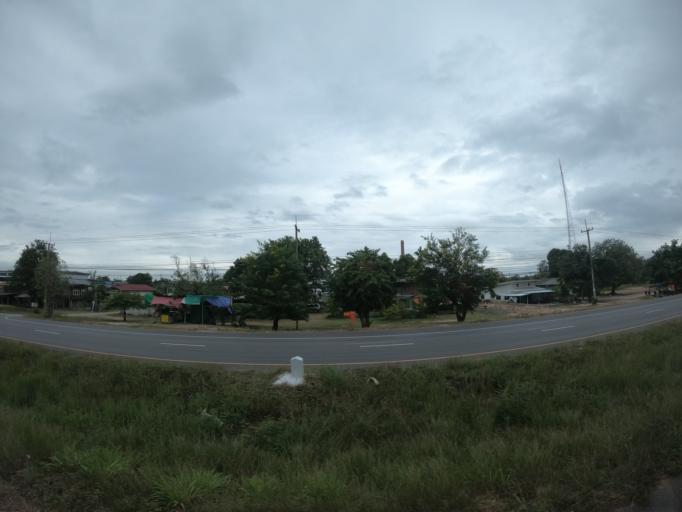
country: TH
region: Roi Et
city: Roi Et
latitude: 16.0738
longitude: 103.5933
